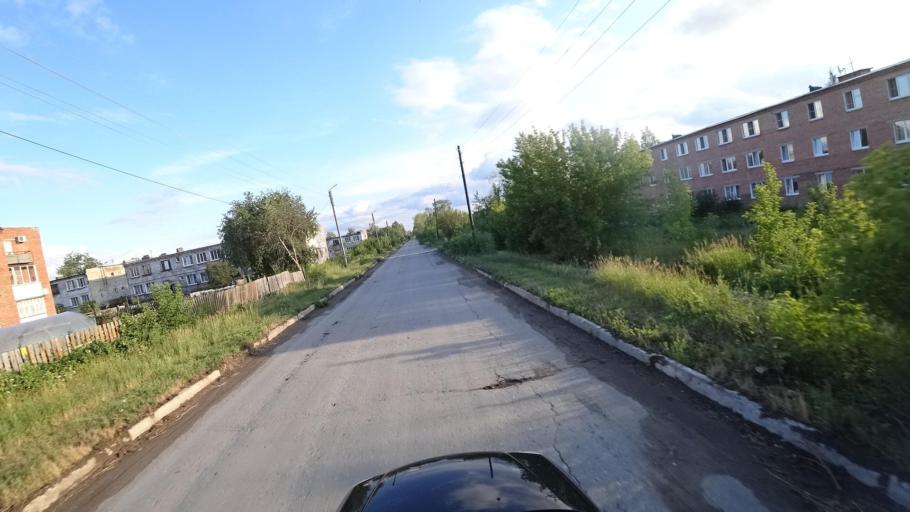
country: RU
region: Sverdlovsk
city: Kamyshlov
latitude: 56.8560
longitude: 62.7308
